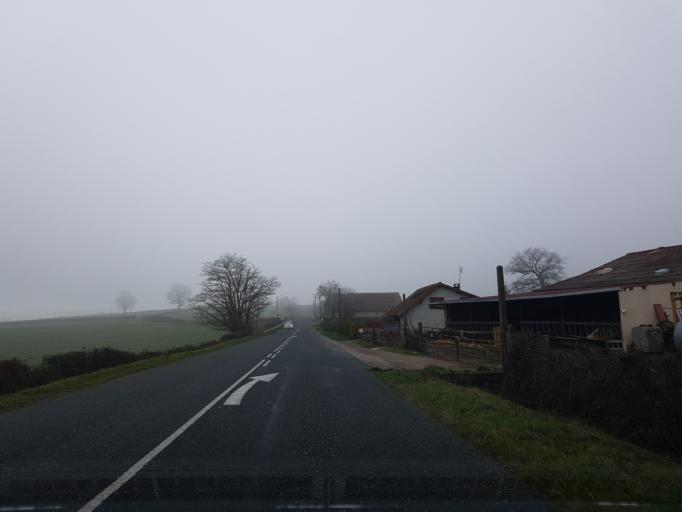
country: FR
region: Bourgogne
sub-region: Departement de Saone-et-Loire
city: Saint-Berain-sous-Sanvignes
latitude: 46.7054
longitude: 4.2198
